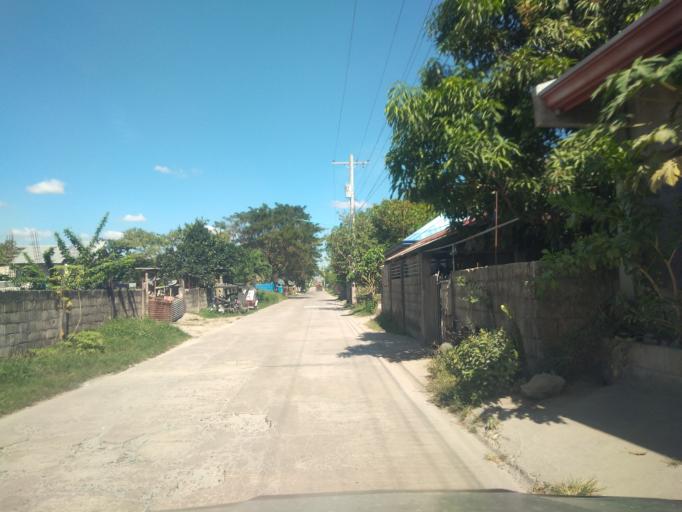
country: PH
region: Central Luzon
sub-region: Province of Pampanga
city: Bacolor
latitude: 15.0139
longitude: 120.6427
